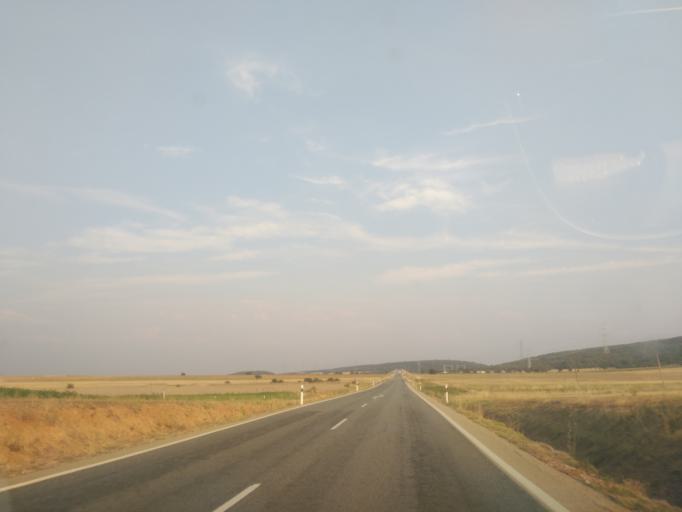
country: ES
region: Castille and Leon
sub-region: Provincia de Zamora
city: Moreruela de Tabara
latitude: 41.7683
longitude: -5.8713
